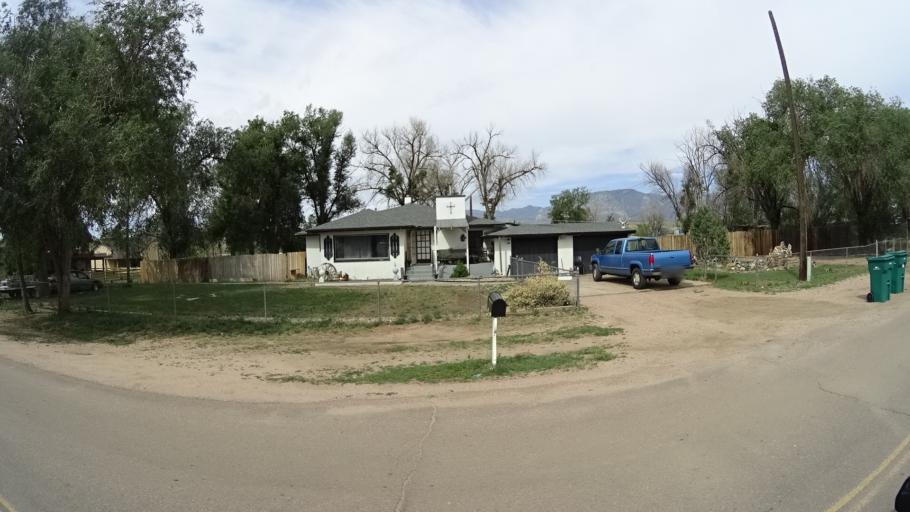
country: US
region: Colorado
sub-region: El Paso County
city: Security-Widefield
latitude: 38.7443
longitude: -104.7409
